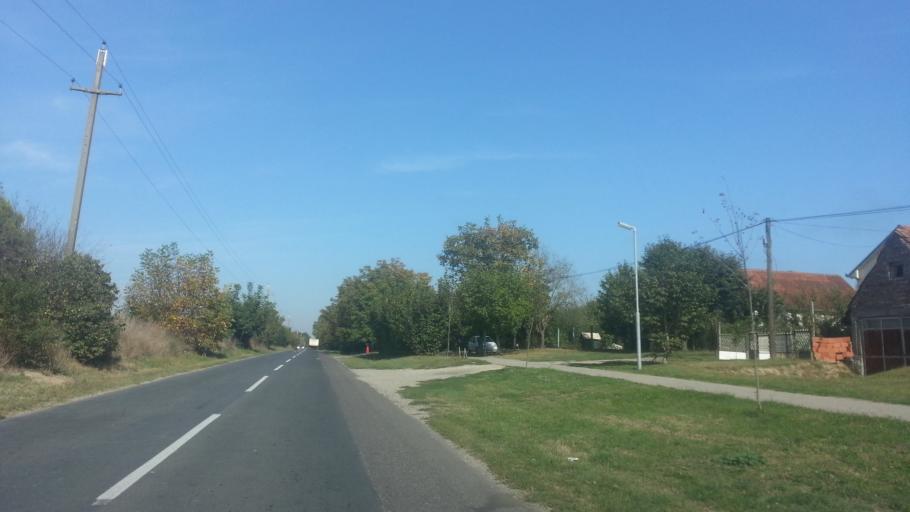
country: RS
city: Stari Banovci
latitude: 44.9973
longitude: 20.2973
